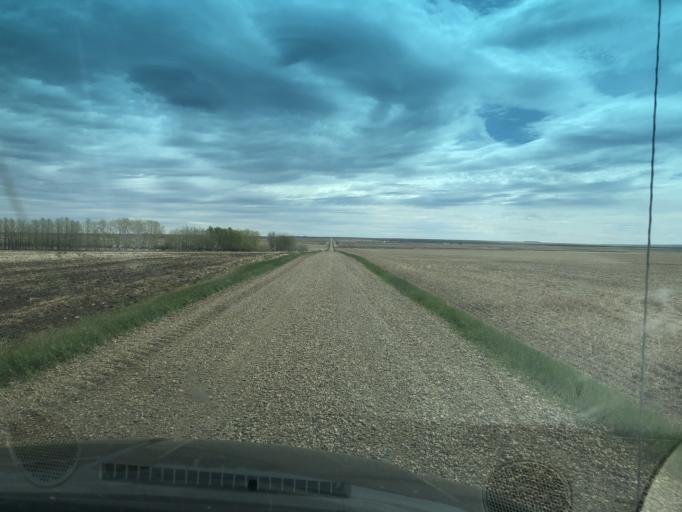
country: CA
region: Alberta
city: Vulcan
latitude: 50.3245
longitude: -113.3533
